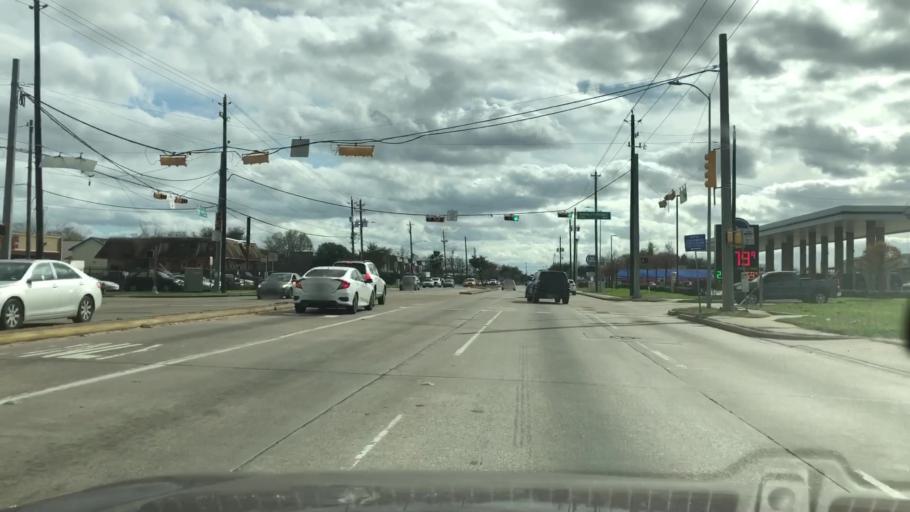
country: US
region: Texas
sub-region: Harris County
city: Bellaire
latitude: 29.6412
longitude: -95.4637
